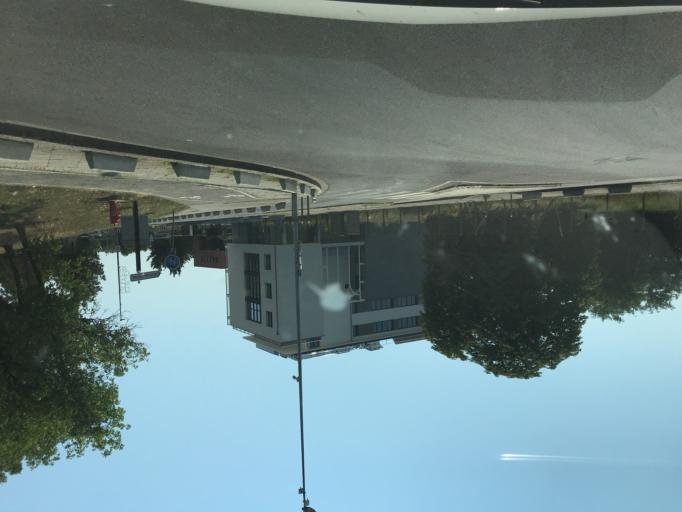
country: FR
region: Rhone-Alpes
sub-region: Departement du Rhone
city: Decines-Charpieu
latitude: 45.7721
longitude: 4.9757
